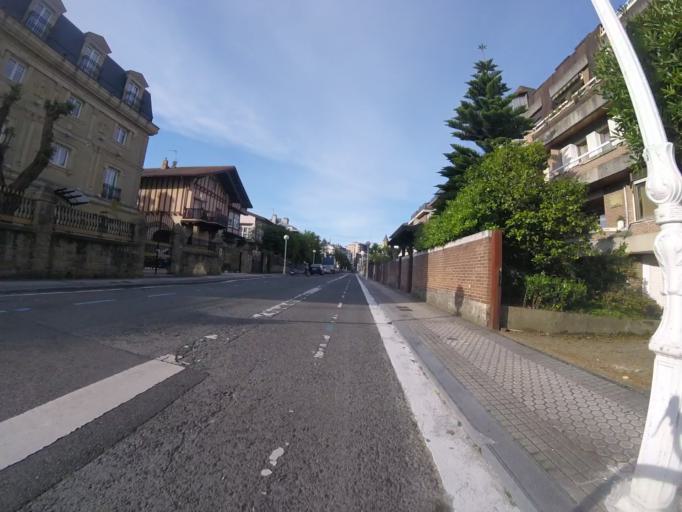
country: ES
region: Basque Country
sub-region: Provincia de Guipuzcoa
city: San Sebastian
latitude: 43.3159
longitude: -2.0036
